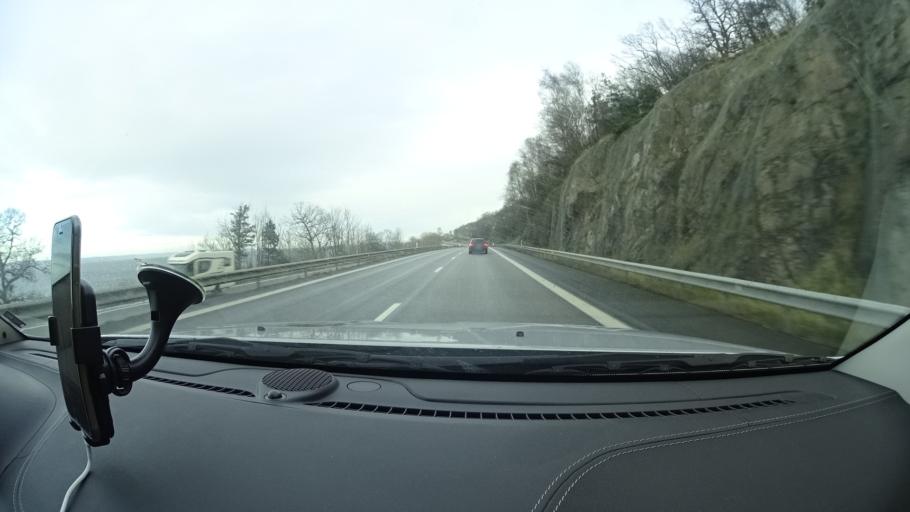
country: SE
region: Joenkoeping
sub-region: Jonkopings Kommun
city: Kaxholmen
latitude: 57.8701
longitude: 14.2723
